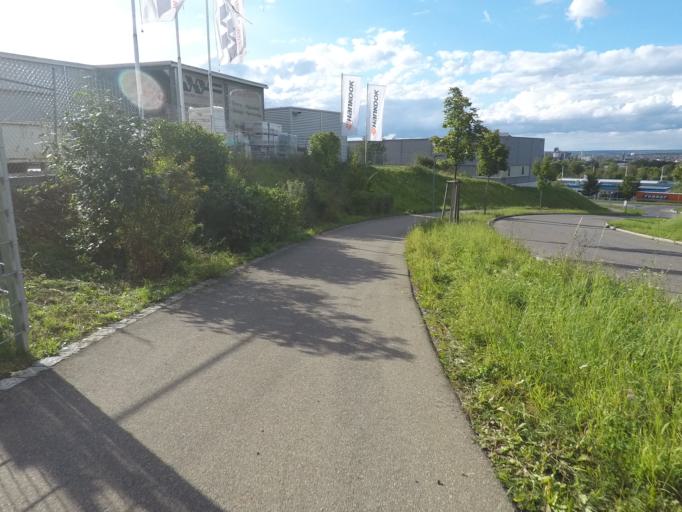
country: DE
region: Baden-Wuerttemberg
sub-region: Tuebingen Region
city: Pfullingen
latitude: 48.4725
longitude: 9.2352
